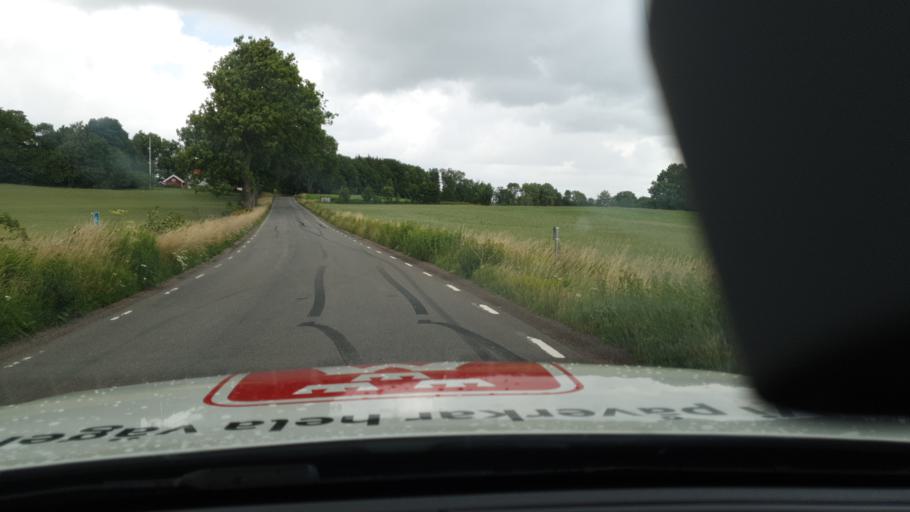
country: SE
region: Vaestra Goetaland
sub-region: Falkopings Kommun
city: Akarp
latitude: 58.2153
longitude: 13.6032
